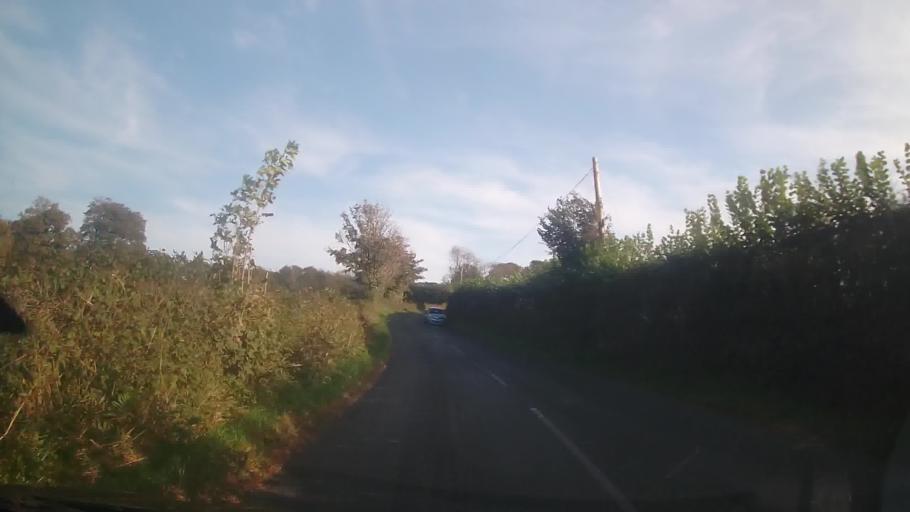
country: GB
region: Wales
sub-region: Pembrokeshire
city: Fishguard
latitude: 51.9784
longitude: -4.9269
